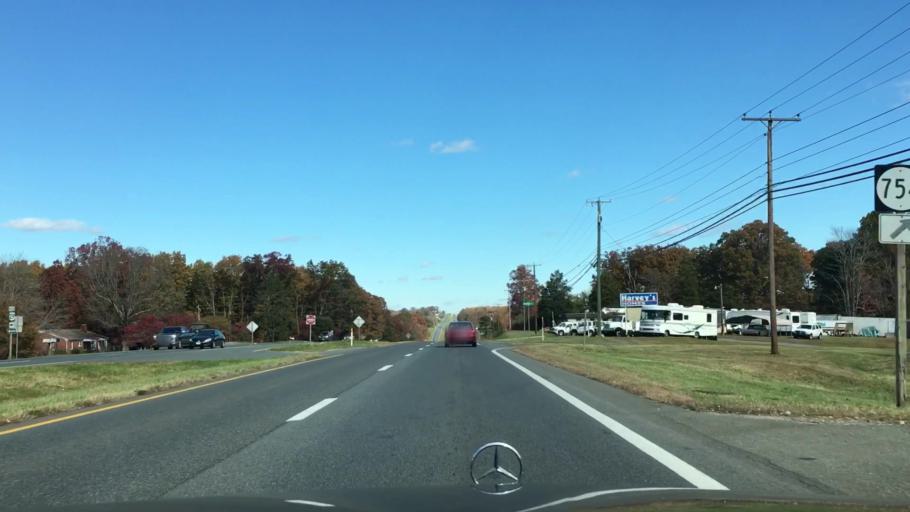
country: US
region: Virginia
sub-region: Campbell County
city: Rustburg
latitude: 37.2561
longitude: -79.1846
